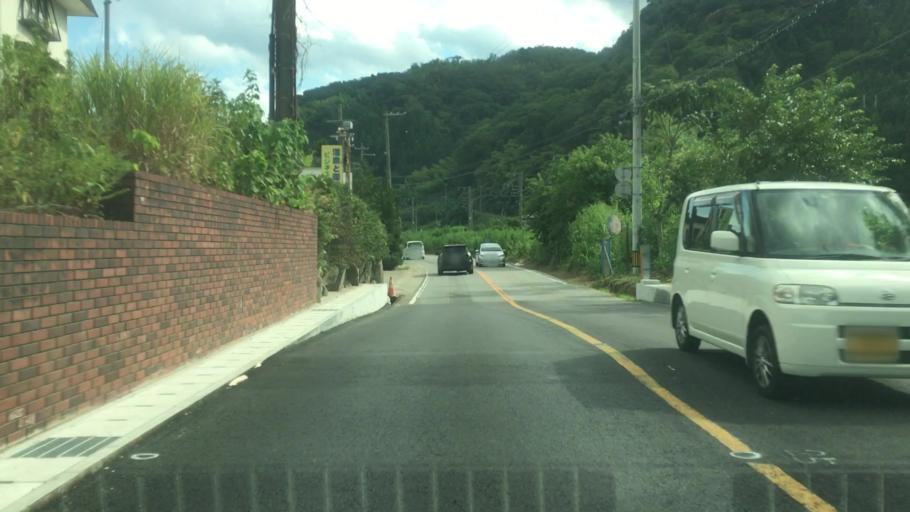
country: JP
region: Hyogo
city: Toyooka
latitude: 35.5913
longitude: 134.7997
